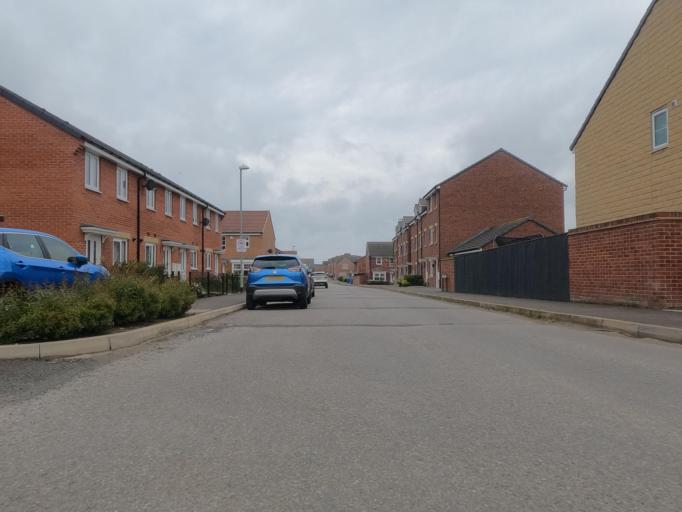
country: GB
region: England
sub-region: Northumberland
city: Blyth
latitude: 55.1210
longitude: -1.5467
